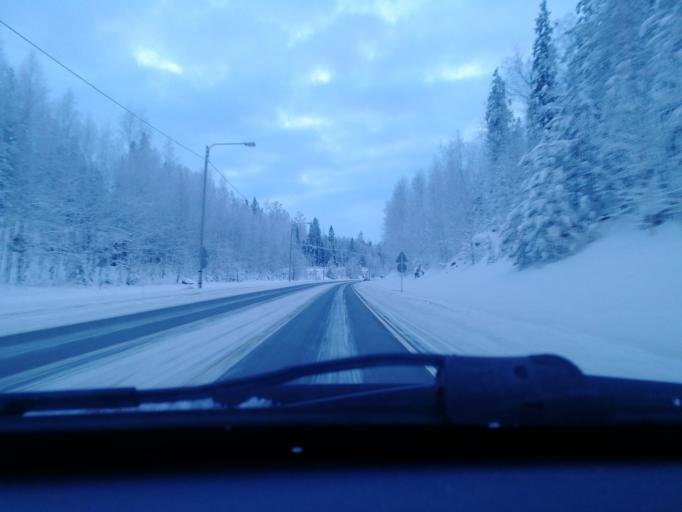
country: FI
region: Pirkanmaa
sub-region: Tampere
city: Tampere
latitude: 61.4383
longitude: 23.8590
